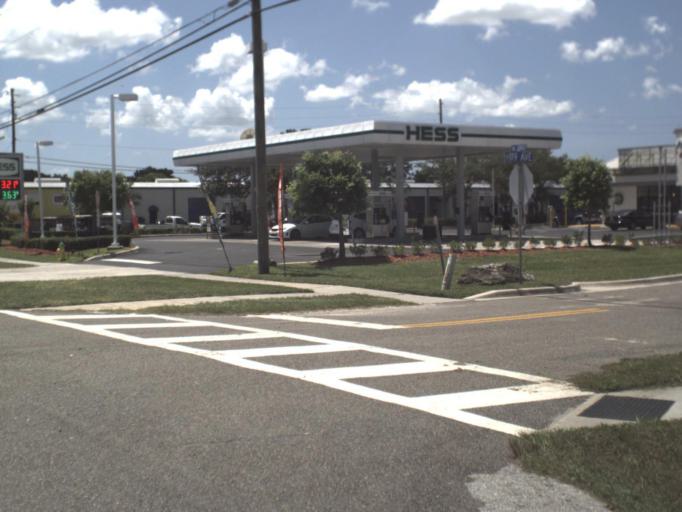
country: US
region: Florida
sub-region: Pinellas County
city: South Highpoint
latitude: 27.8799
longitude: -82.7292
